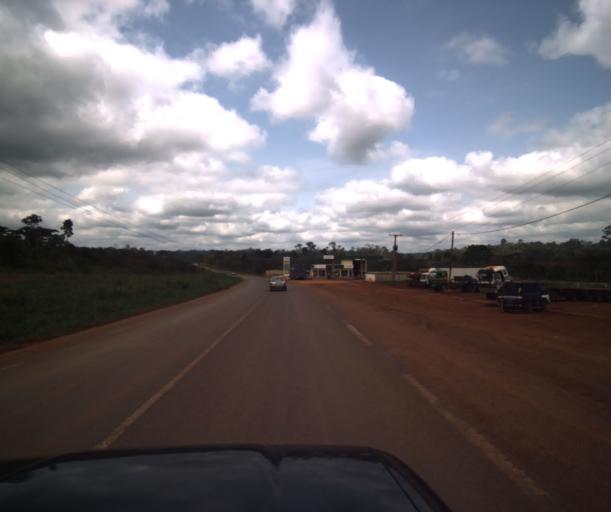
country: CM
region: Centre
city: Yaounde
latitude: 3.7936
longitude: 11.4748
